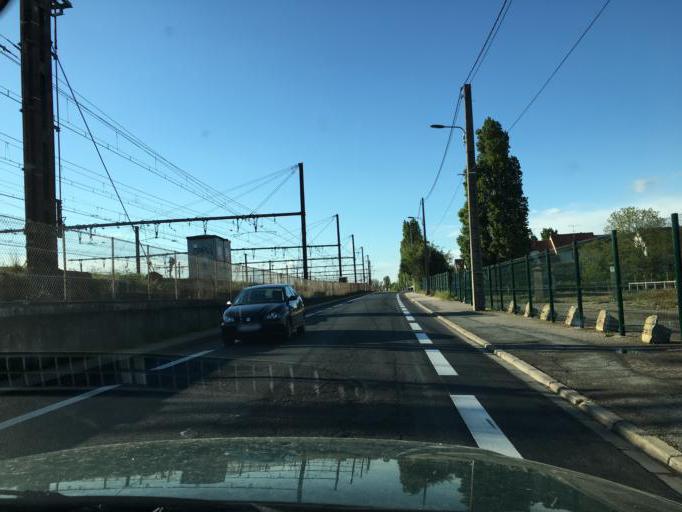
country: FR
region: Centre
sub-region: Departement du Loiret
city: Fleury-les-Aubrais
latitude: 47.9303
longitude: 1.9051
